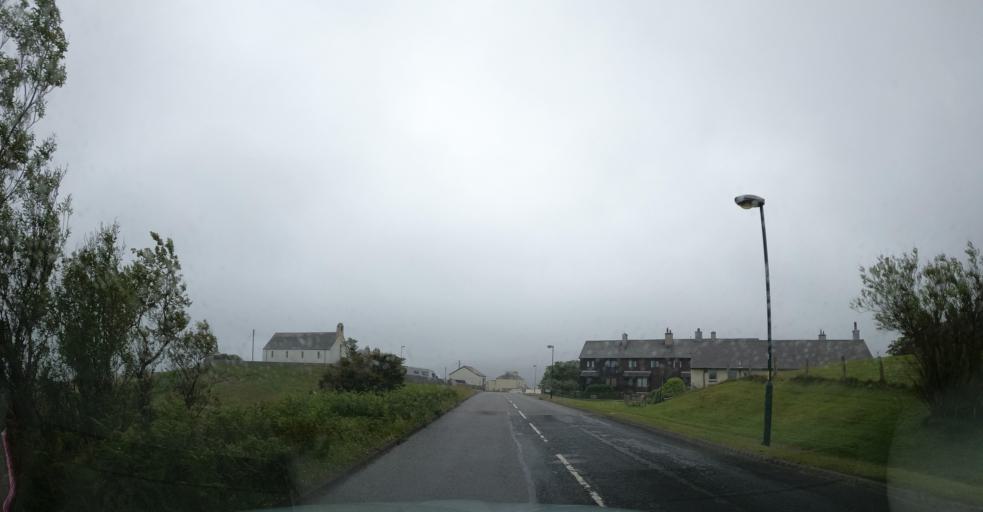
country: GB
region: Scotland
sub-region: Eilean Siar
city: Isle of North Uist
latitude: 57.6009
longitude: -7.1621
